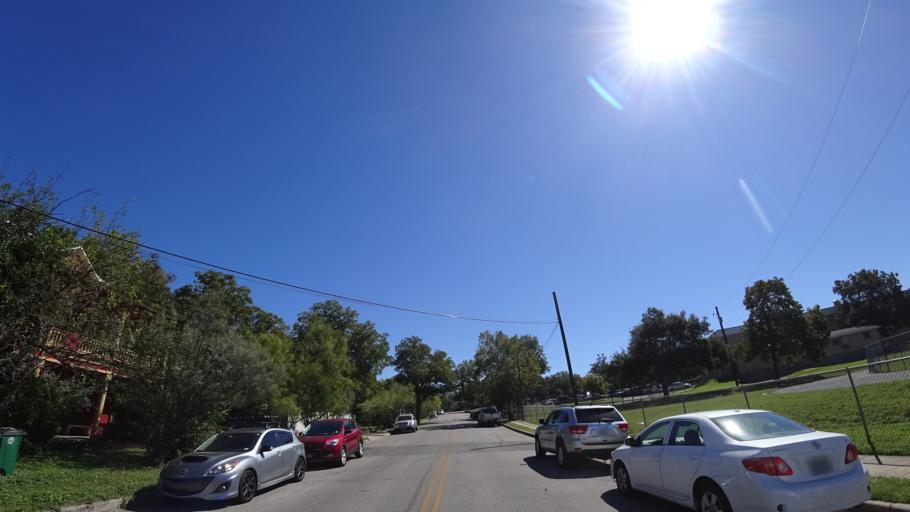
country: US
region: Texas
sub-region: Travis County
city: Austin
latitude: 30.2450
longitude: -97.7507
